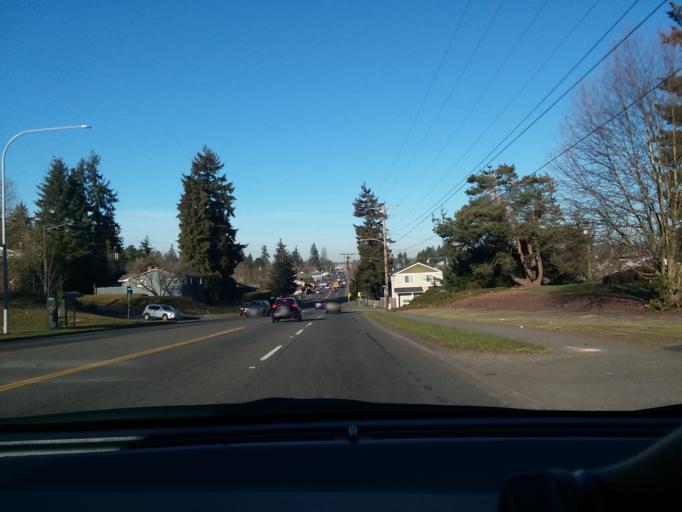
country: US
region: Washington
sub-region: Pierce County
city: Parkland
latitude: 47.1902
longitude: -122.4676
